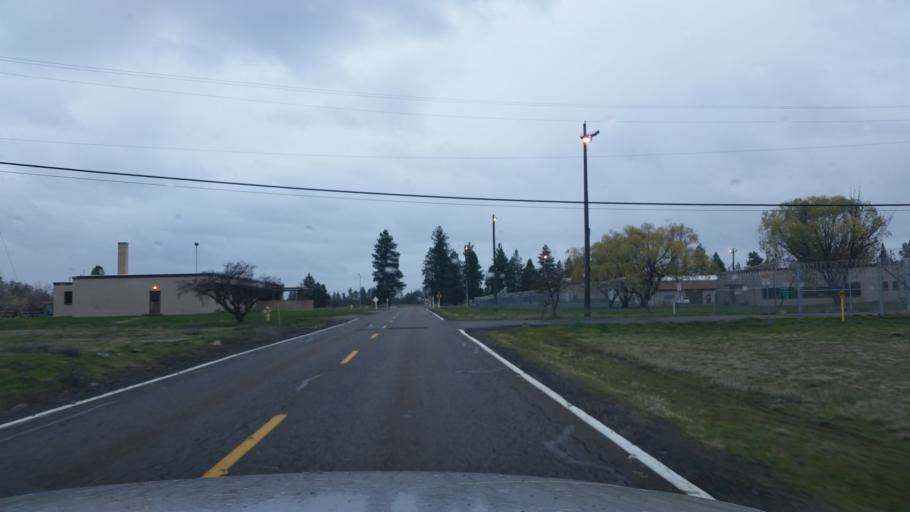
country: US
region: Washington
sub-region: Spokane County
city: Airway Heights
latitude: 47.6230
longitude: -117.5133
